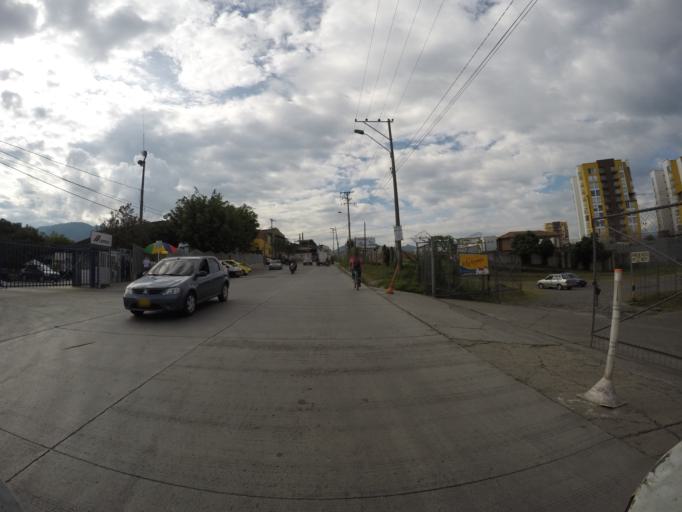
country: CO
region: Risaralda
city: Pereira
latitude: 4.8218
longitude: -75.6889
